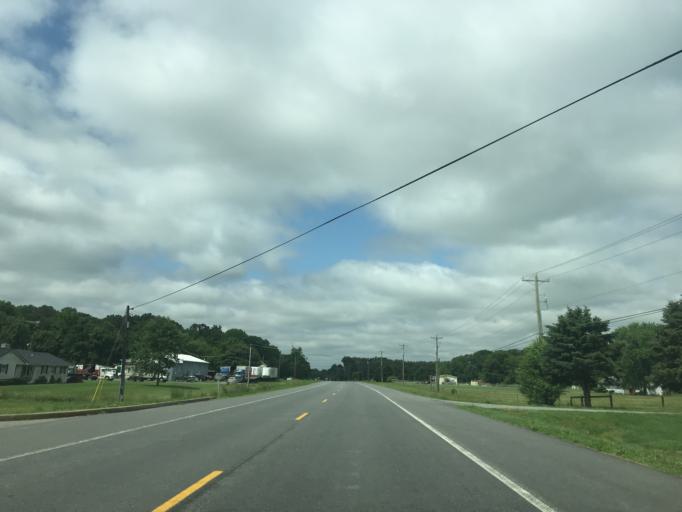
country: US
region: Maryland
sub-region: Caroline County
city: Ridgely
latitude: 38.9268
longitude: -75.9238
